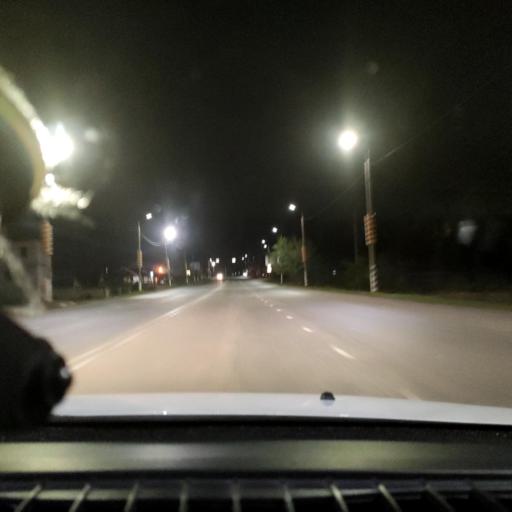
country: RU
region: Samara
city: Novokuybyshevsk
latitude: 53.0817
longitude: 49.9597
